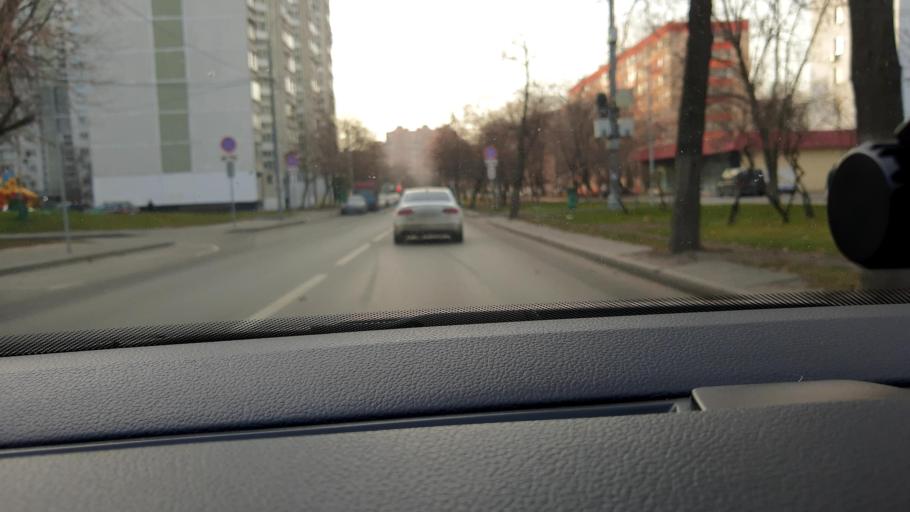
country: RU
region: Moscow
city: Novokuz'minki
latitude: 55.7127
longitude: 37.7812
